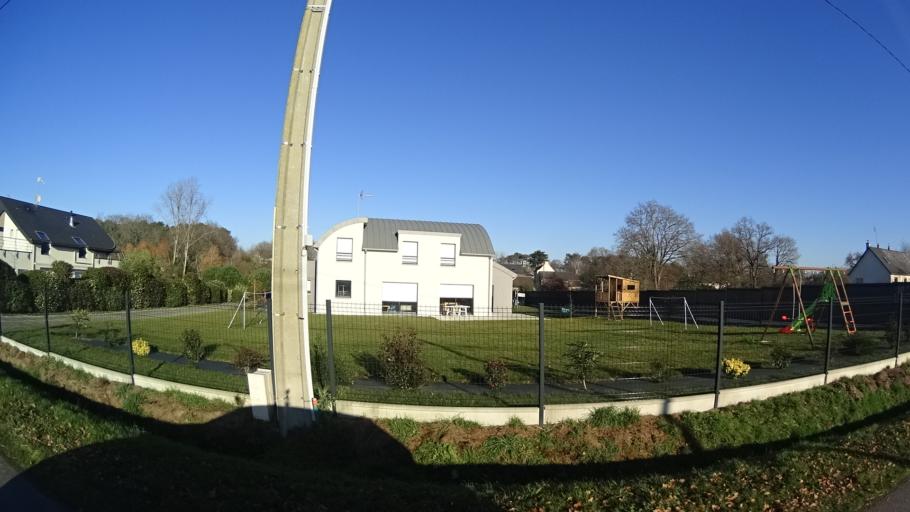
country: FR
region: Brittany
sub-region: Departement du Morbihan
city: Allaire
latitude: 47.6418
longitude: -2.1747
